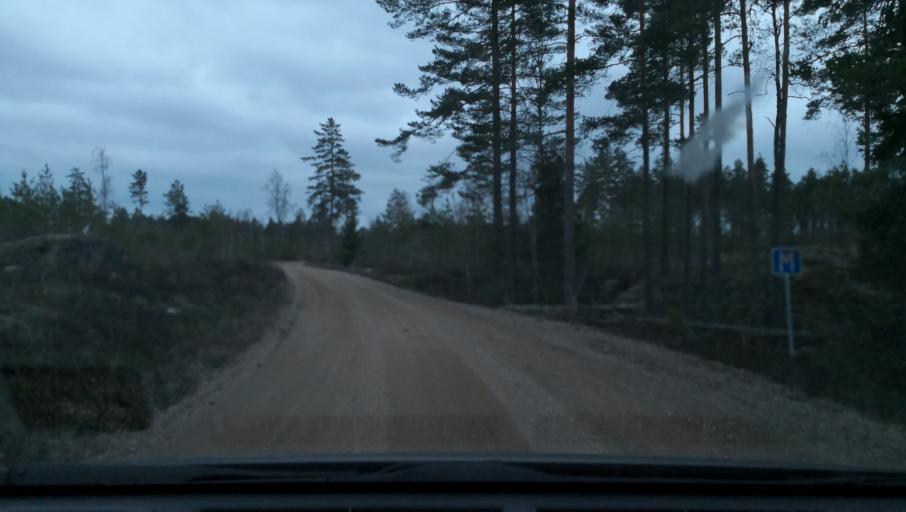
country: SE
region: OErebro
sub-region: Lindesbergs Kommun
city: Fellingsbro
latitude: 59.6054
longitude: 15.5775
